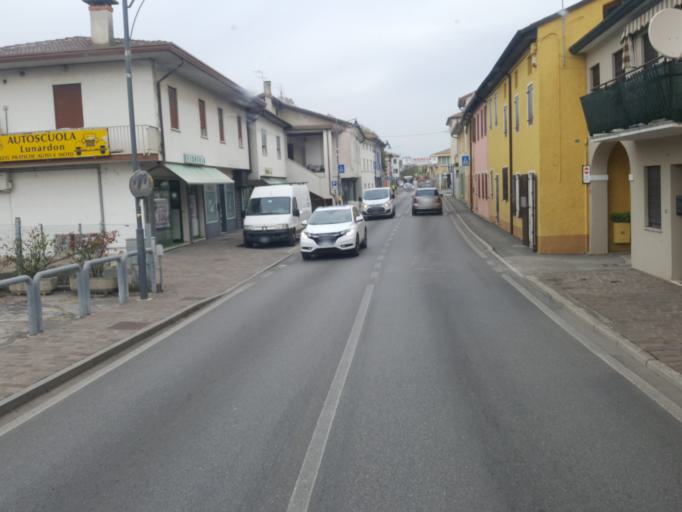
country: IT
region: Veneto
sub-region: Provincia di Treviso
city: Loria Bessica
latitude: 45.7273
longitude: 11.8654
